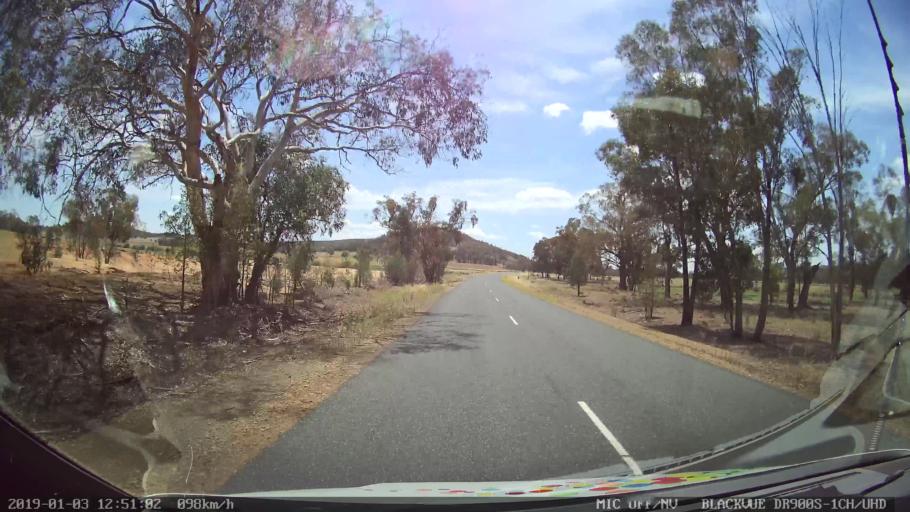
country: AU
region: New South Wales
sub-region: Weddin
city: Grenfell
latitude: -33.6842
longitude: 148.2759
